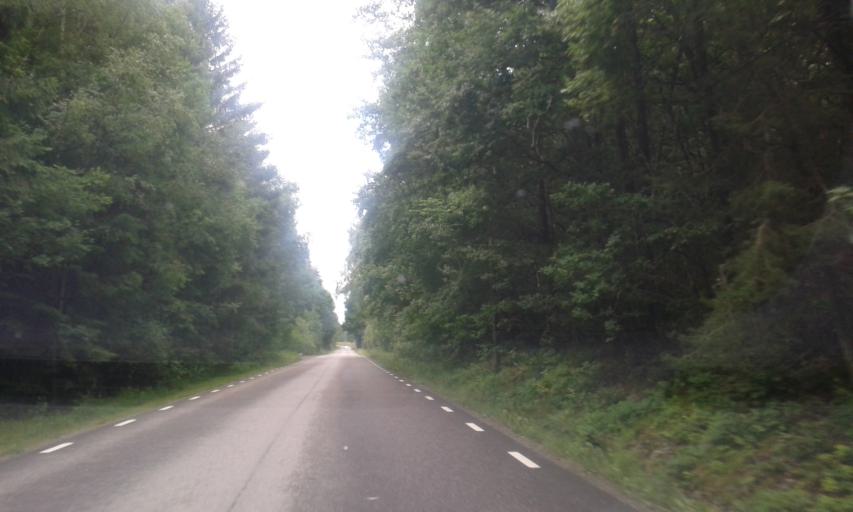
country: SE
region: Vaestra Goetaland
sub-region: Kungalvs Kommun
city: Kode
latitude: 57.8981
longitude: 11.8969
